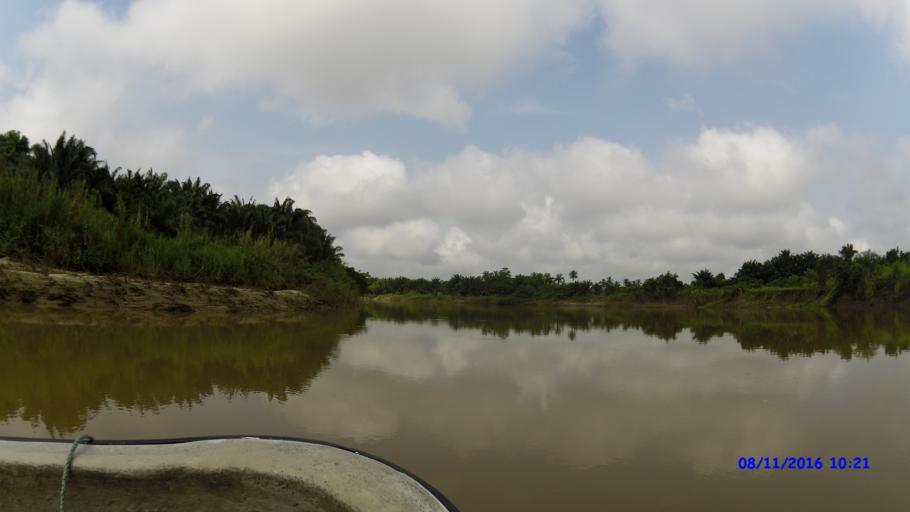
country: BJ
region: Mono
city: Come
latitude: 6.4068
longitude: 1.7757
